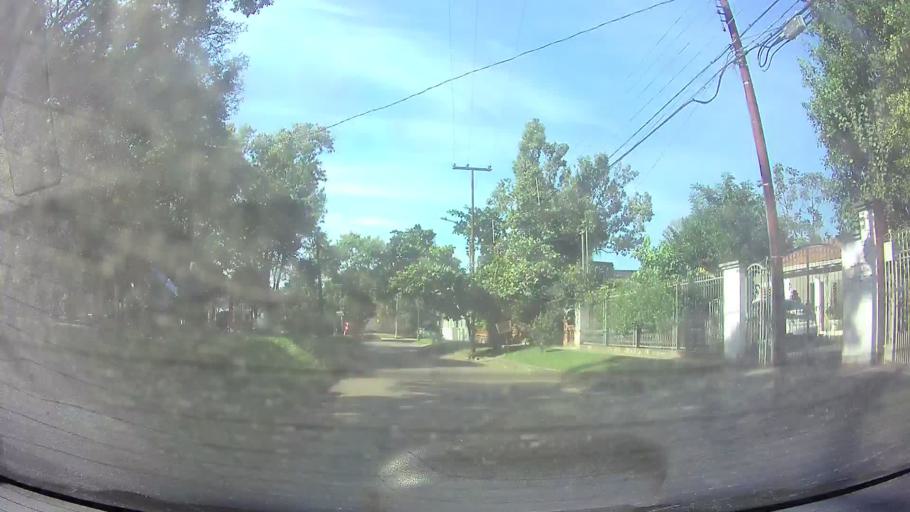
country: PY
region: Central
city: Fernando de la Mora
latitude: -25.2813
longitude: -57.5437
